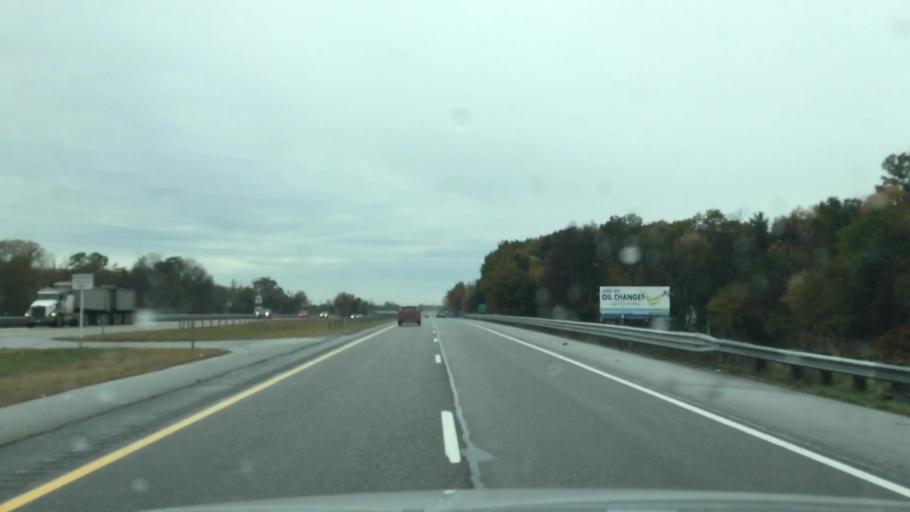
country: US
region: Michigan
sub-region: Calhoun County
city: Albion
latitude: 42.2645
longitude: -84.7448
